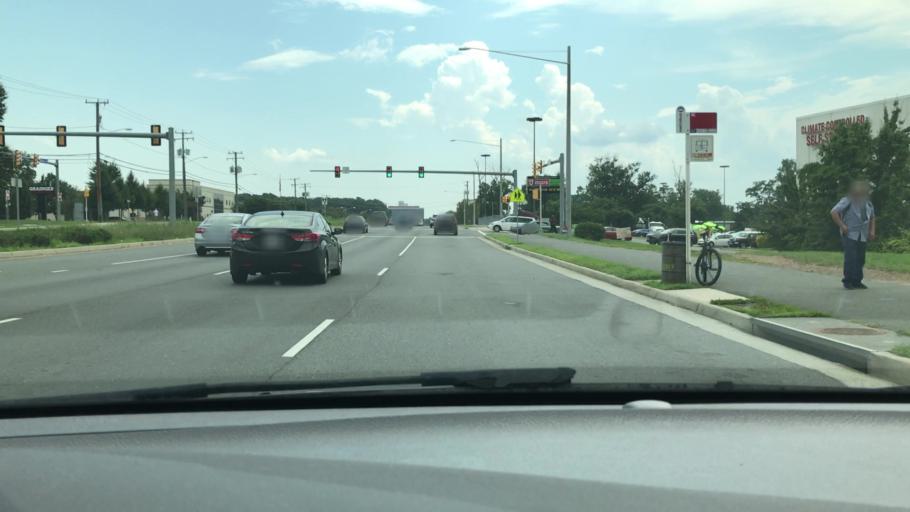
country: US
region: Virginia
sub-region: Fairfax County
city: Merrifield
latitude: 38.8712
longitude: -77.2274
